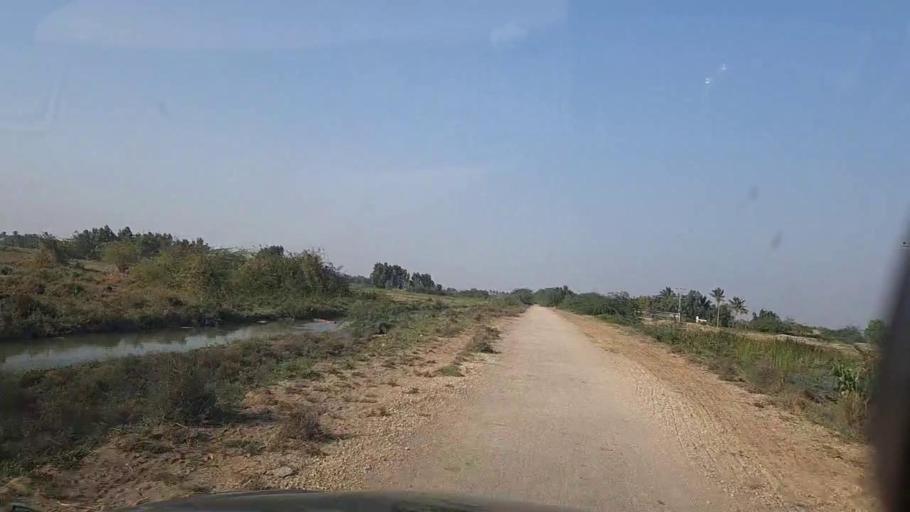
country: PK
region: Sindh
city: Thatta
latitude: 24.6156
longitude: 67.8762
